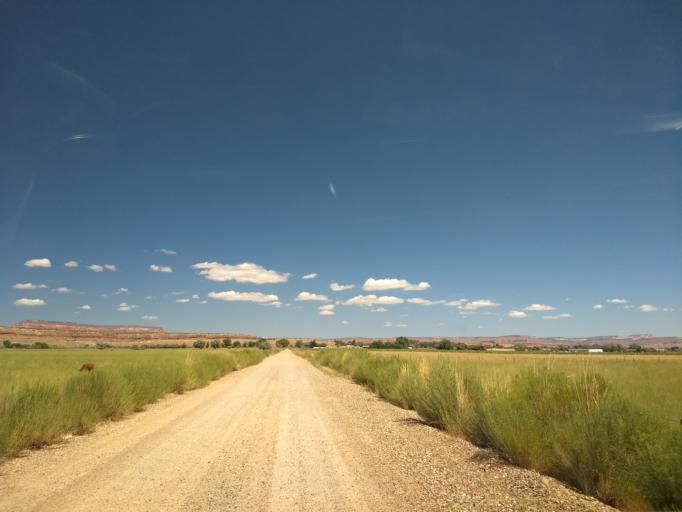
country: US
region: Arizona
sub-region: Coconino County
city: Fredonia
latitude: 36.9264
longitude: -112.5398
